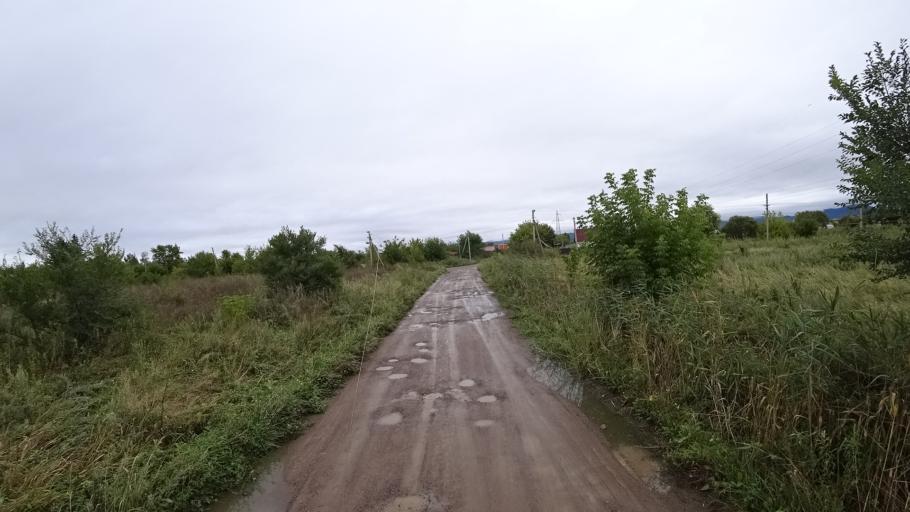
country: RU
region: Primorskiy
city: Monastyrishche
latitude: 44.1998
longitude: 132.4731
